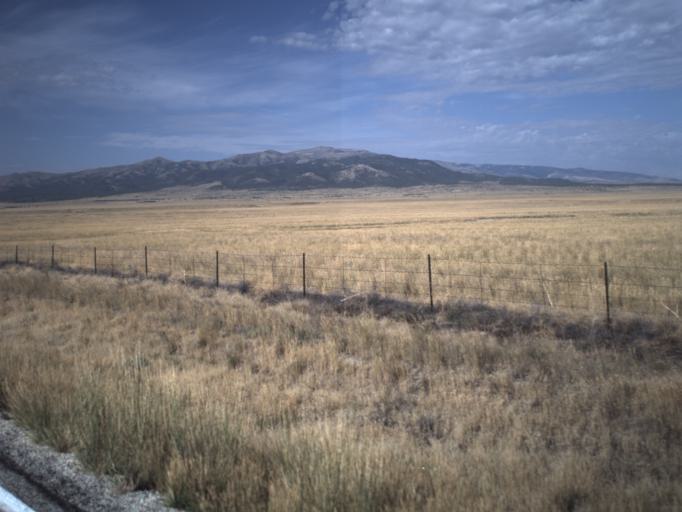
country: US
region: Idaho
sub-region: Oneida County
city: Malad City
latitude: 41.9534
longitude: -113.0743
